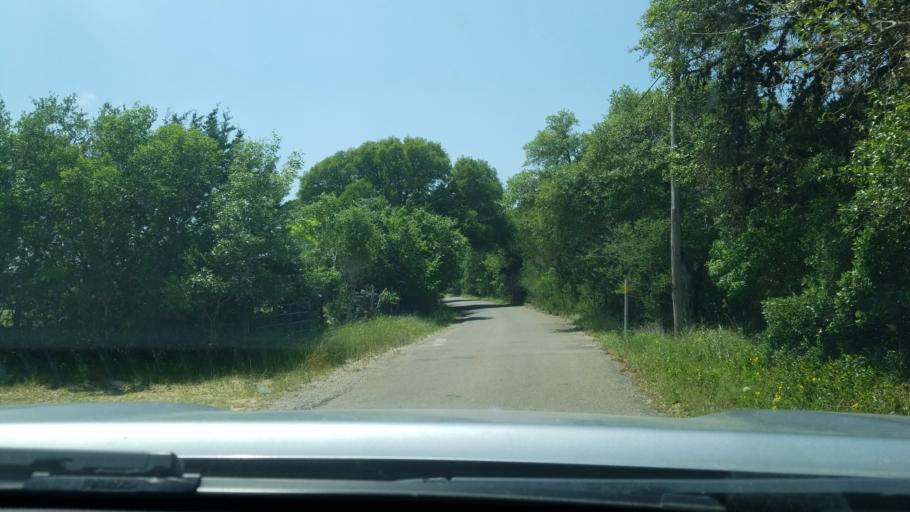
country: US
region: Texas
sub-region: Blanco County
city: Blanco
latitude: 30.0011
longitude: -98.4095
